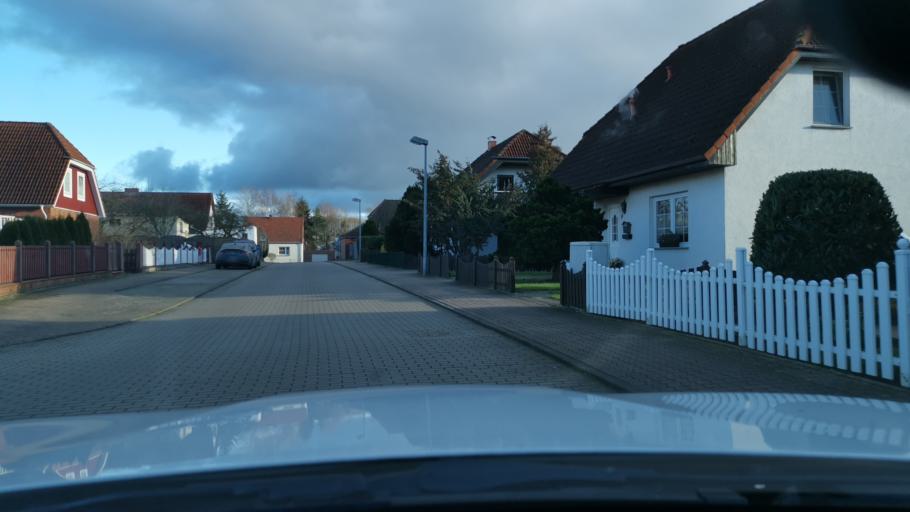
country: DE
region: Mecklenburg-Vorpommern
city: Tessin
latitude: 54.0258
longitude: 12.4558
